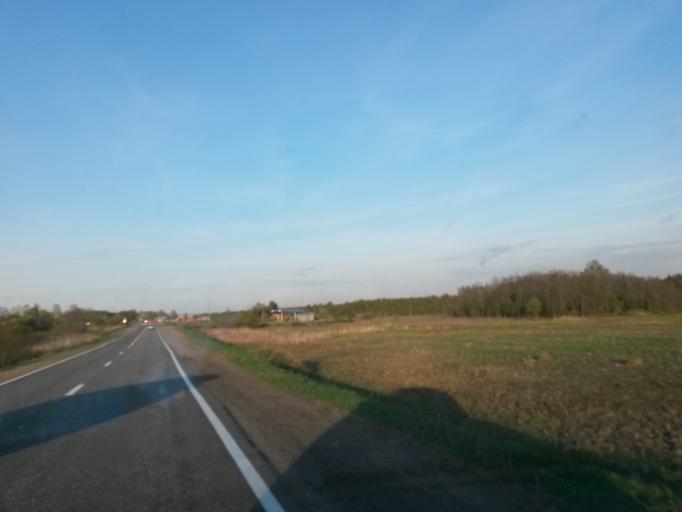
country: RU
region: Jaroslavl
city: Kurba
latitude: 57.6794
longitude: 39.4545
